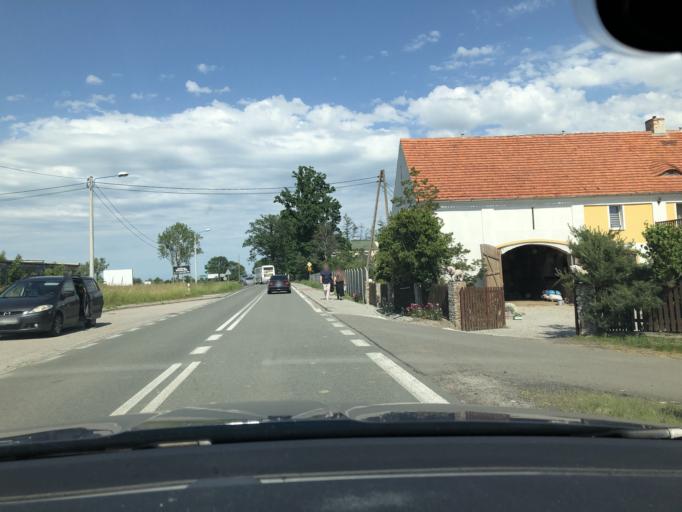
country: PL
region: Lower Silesian Voivodeship
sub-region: Powiat jaworski
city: Paszowice
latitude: 50.9776
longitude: 16.1598
